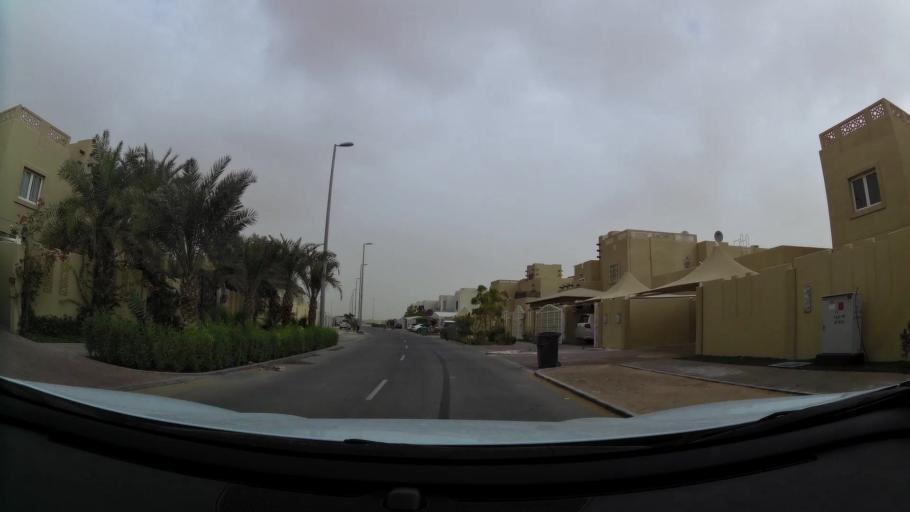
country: AE
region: Abu Dhabi
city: Abu Dhabi
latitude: 24.4587
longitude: 54.7143
